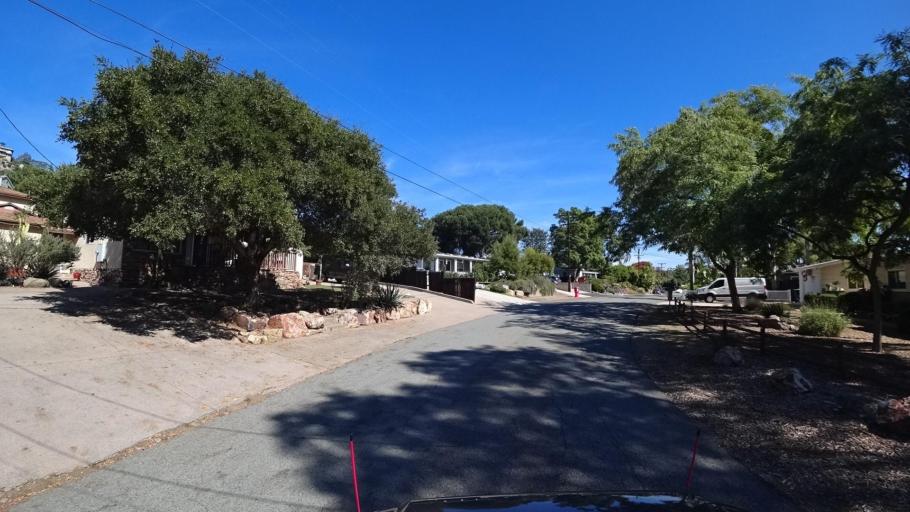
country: US
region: California
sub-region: San Diego County
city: Casa de Oro-Mount Helix
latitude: 32.7545
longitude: -116.9712
